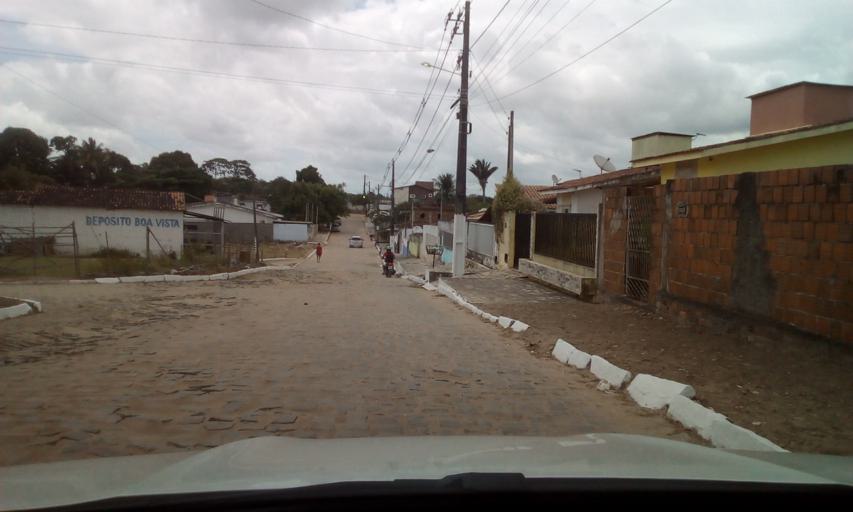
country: BR
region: Paraiba
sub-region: Bayeux
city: Bayeux
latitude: -7.1357
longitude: -34.9526
